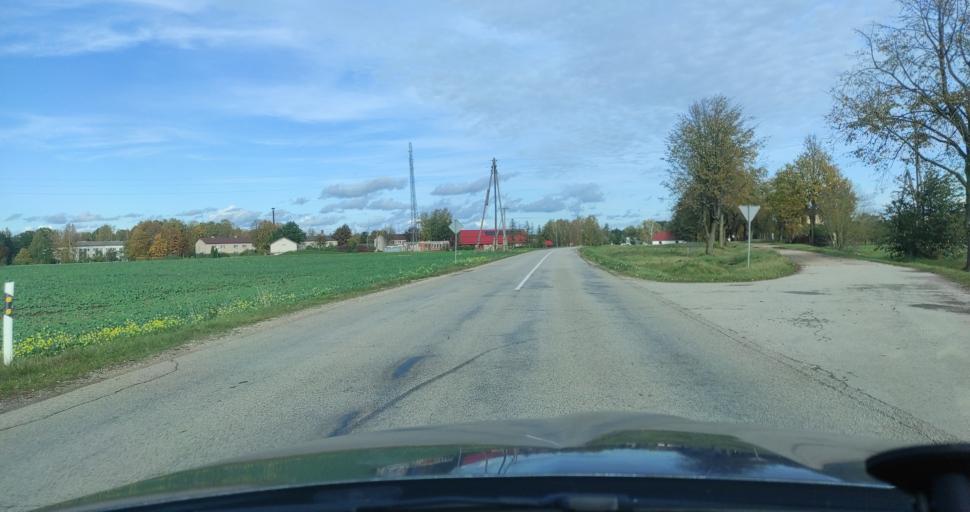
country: LV
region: Jaunpils
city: Jaunpils
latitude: 56.7266
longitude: 23.0087
